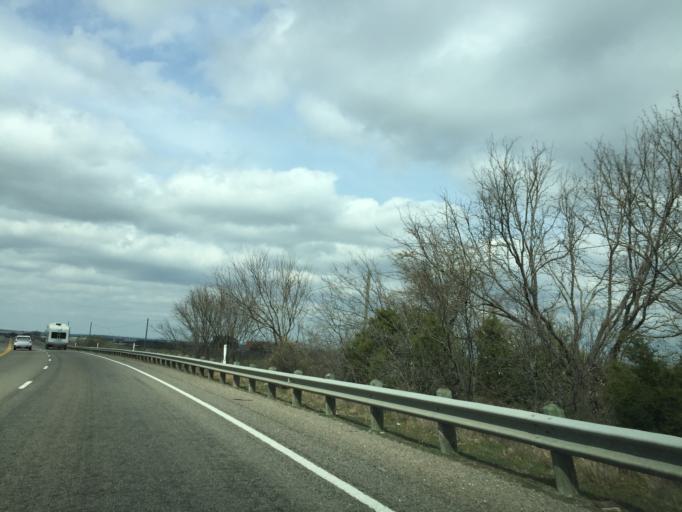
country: US
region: Texas
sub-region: Travis County
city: Briarcliff
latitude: 30.4525
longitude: -98.1492
